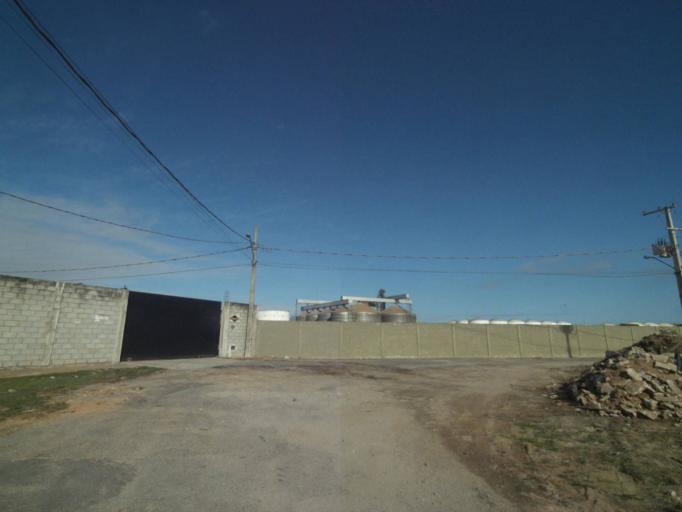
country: BR
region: Parana
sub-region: Paranagua
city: Paranagua
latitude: -25.5110
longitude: -48.5249
